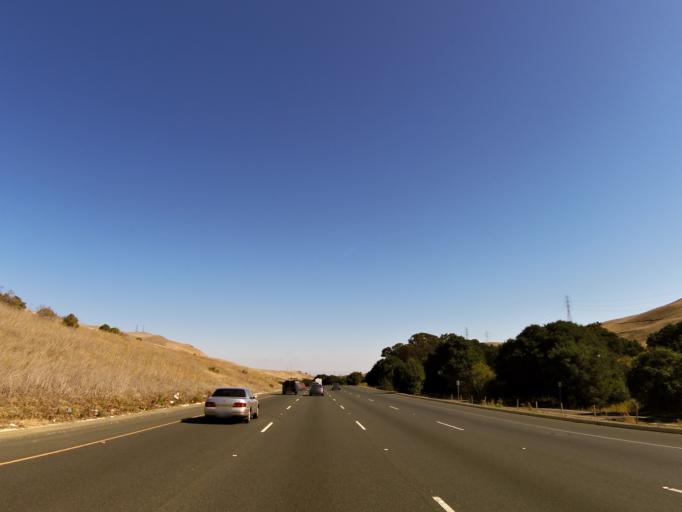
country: US
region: California
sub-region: Napa County
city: American Canyon
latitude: 38.1795
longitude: -122.1878
